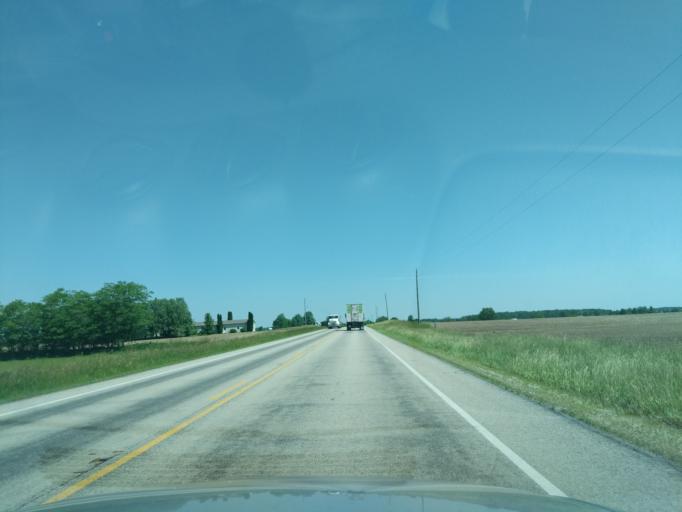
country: US
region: Indiana
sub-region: Huntington County
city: Huntington
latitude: 40.9786
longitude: -85.4716
